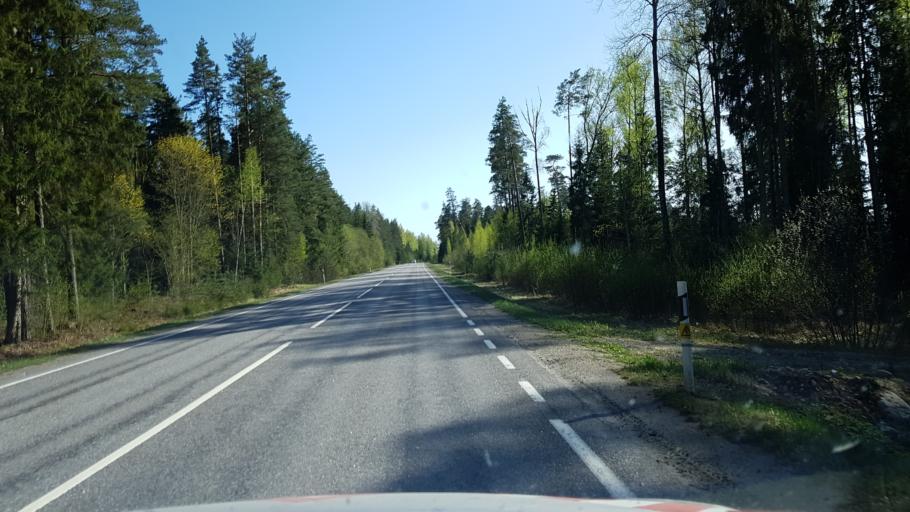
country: EE
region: Paernumaa
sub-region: Saarde vald
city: Kilingi-Nomme
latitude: 58.1889
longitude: 25.0550
